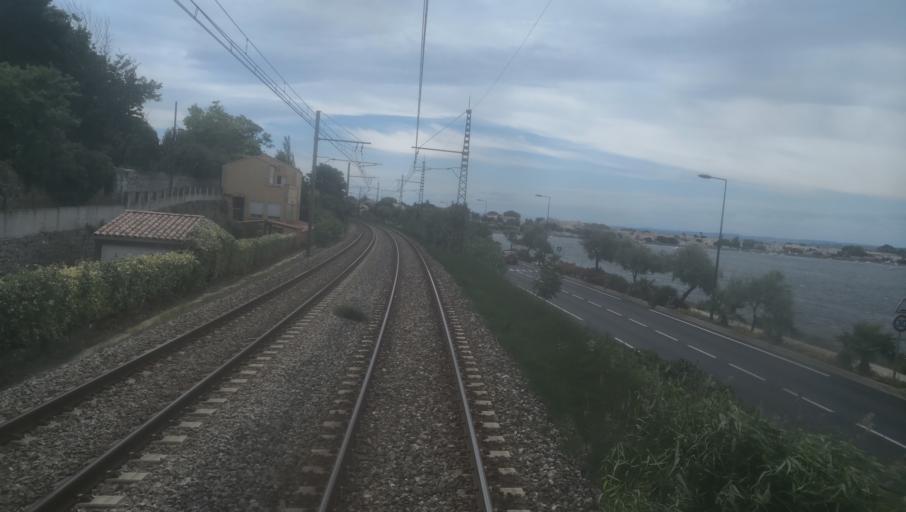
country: FR
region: Languedoc-Roussillon
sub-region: Departement de l'Herault
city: Sete
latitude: 43.4140
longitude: 3.6788
